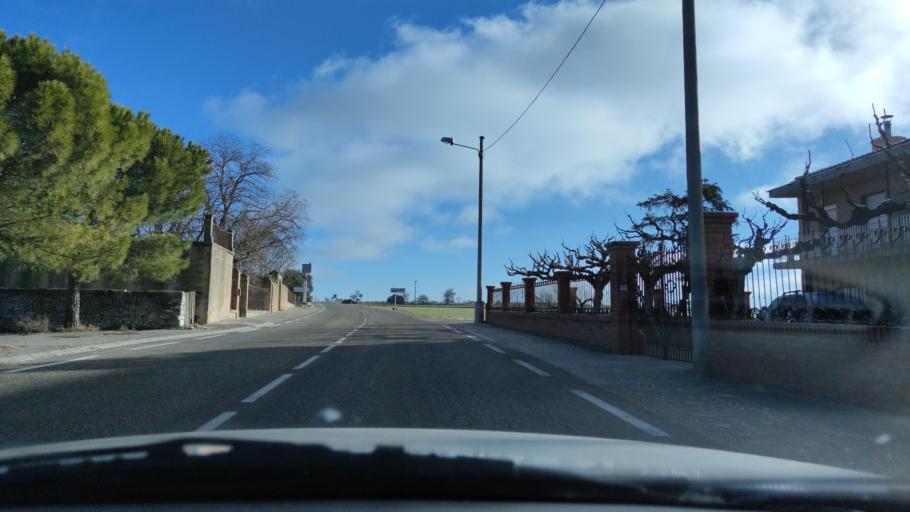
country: ES
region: Catalonia
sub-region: Provincia de Lleida
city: Ivorra
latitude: 41.7266
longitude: 1.3732
